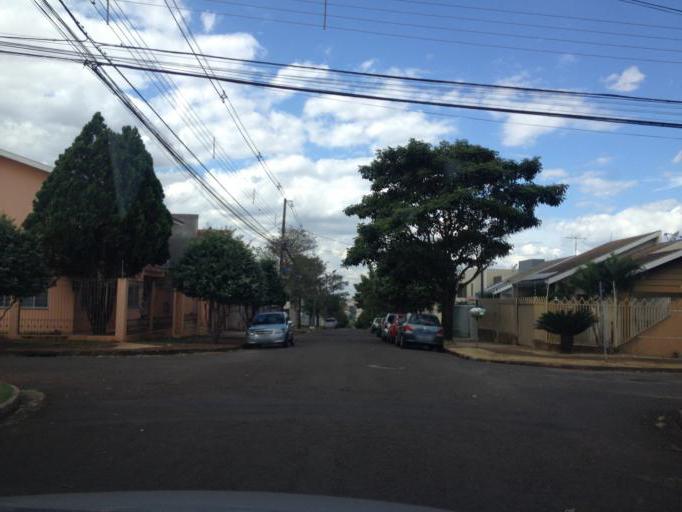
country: BR
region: Parana
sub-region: Maringa
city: Maringa
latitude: -23.4469
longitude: -51.9513
